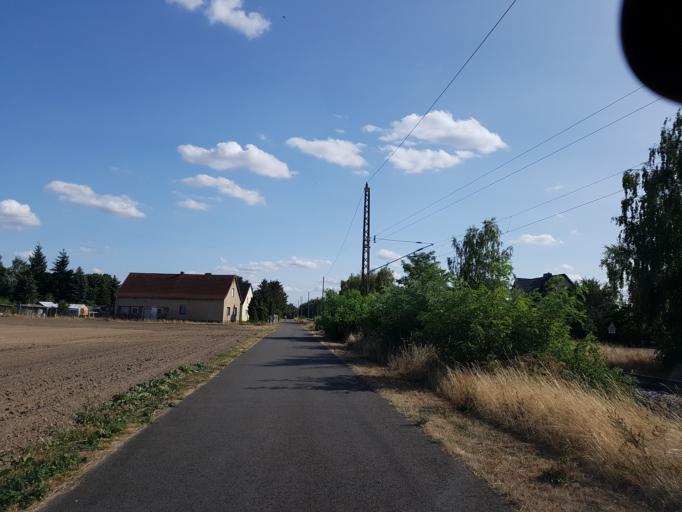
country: DE
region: Brandenburg
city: Juterbog
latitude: 51.8958
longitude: 13.0664
